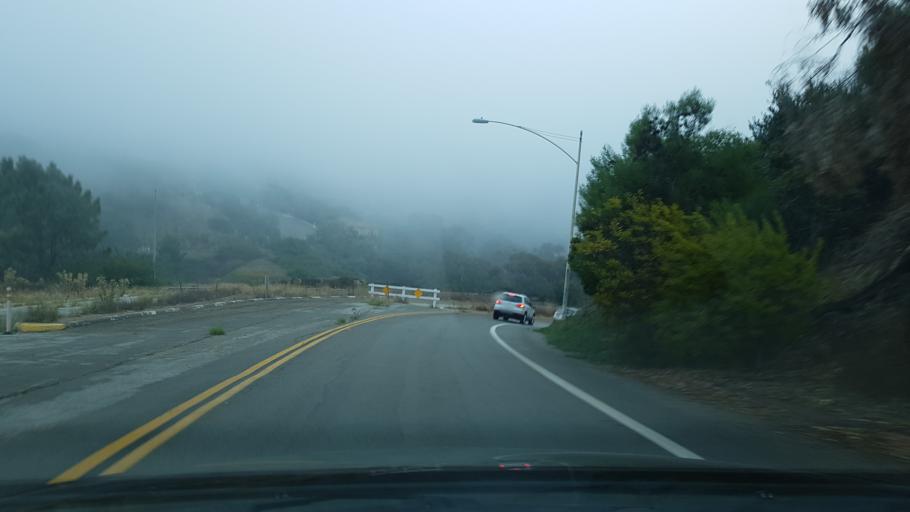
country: US
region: California
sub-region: San Diego County
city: La Jolla
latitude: 32.8476
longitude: -117.2430
